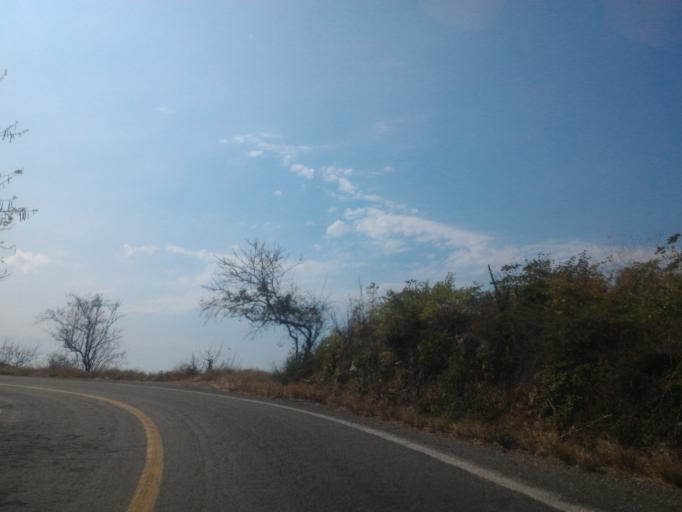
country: MX
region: Michoacan
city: Coahuayana Viejo
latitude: 18.4901
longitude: -103.5740
